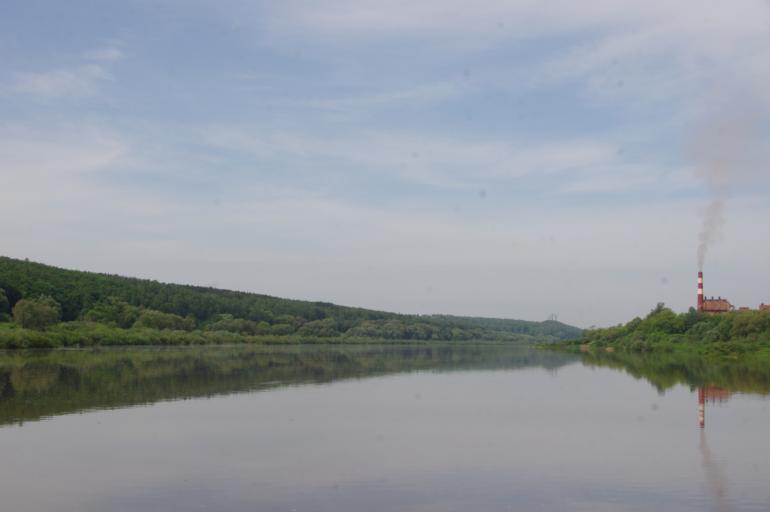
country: RU
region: Tula
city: Aleksin
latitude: 54.4903
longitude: 37.0751
